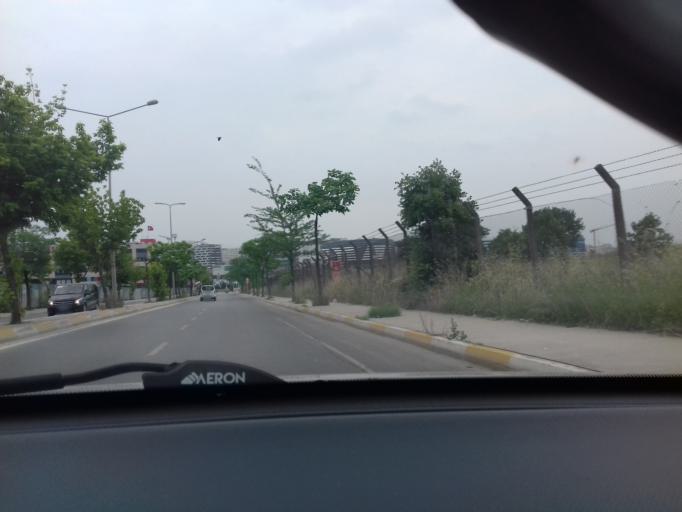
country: TR
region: Istanbul
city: Sultanbeyli
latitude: 40.9203
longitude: 29.3086
